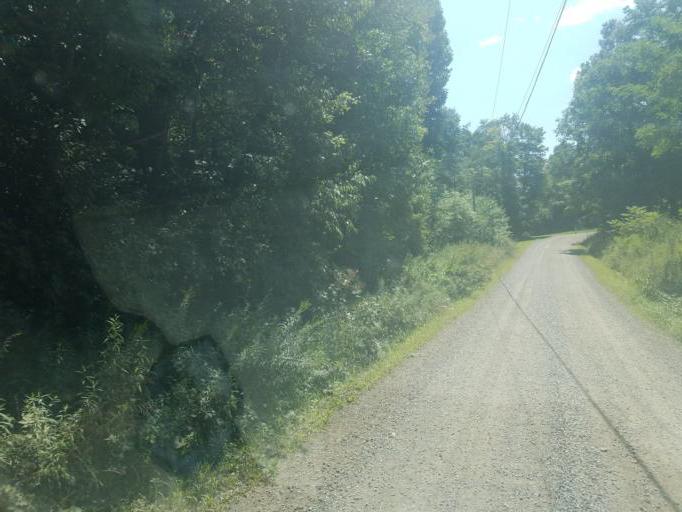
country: US
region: Pennsylvania
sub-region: Clarion County
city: Knox
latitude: 41.2076
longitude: -79.5765
